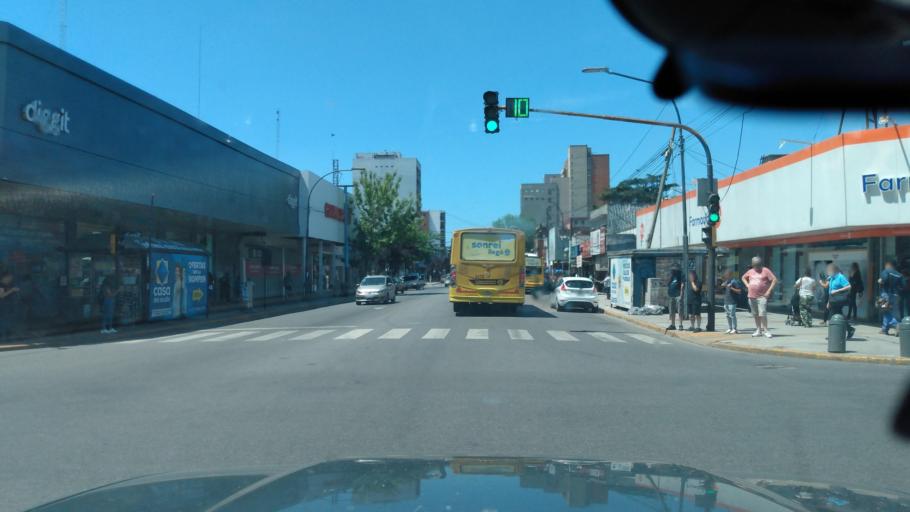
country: AR
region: Buenos Aires
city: Hurlingham
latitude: -34.5423
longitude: -58.7120
